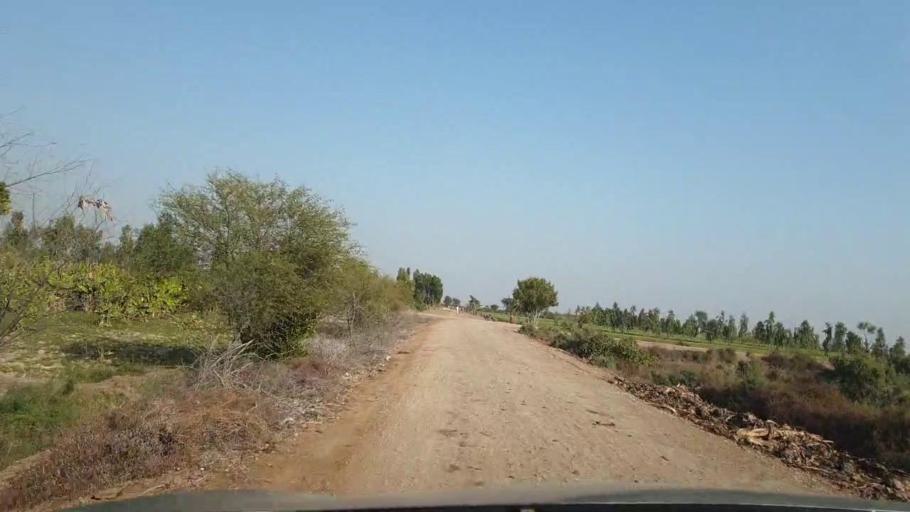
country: PK
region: Sindh
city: Berani
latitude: 25.6849
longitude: 68.8199
